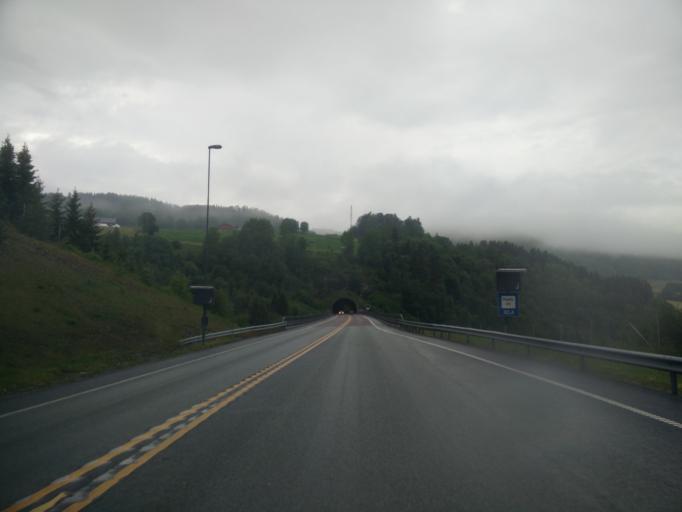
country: NO
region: Sor-Trondelag
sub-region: Skaun
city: Borsa
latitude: 63.3299
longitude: 9.9979
